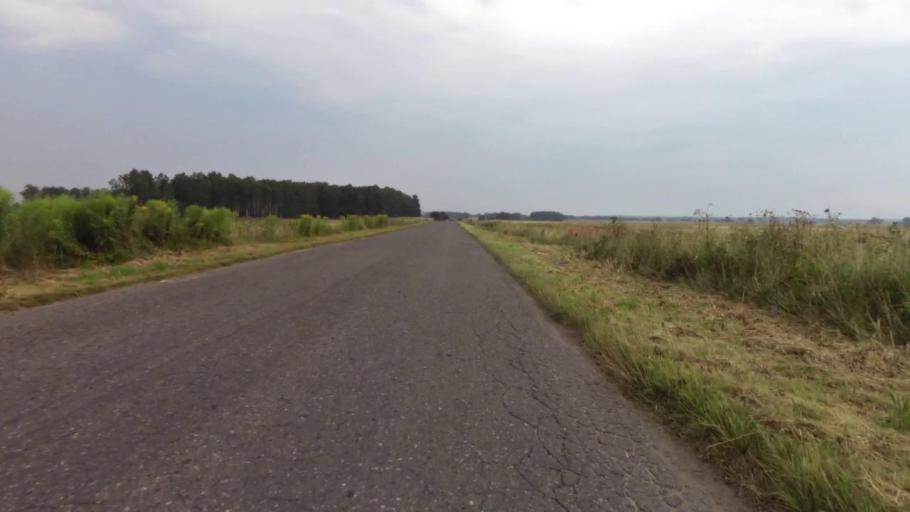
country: PL
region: West Pomeranian Voivodeship
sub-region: Powiat lobeski
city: Wegorzyno
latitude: 53.4963
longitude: 15.6330
